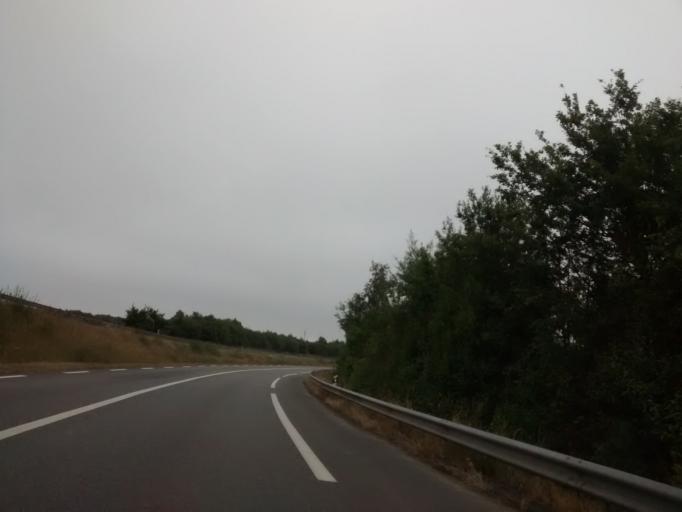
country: FR
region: Brittany
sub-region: Departement d'Ille-et-Vilaine
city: Cesson-Sevigne
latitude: 48.1141
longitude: -1.5772
